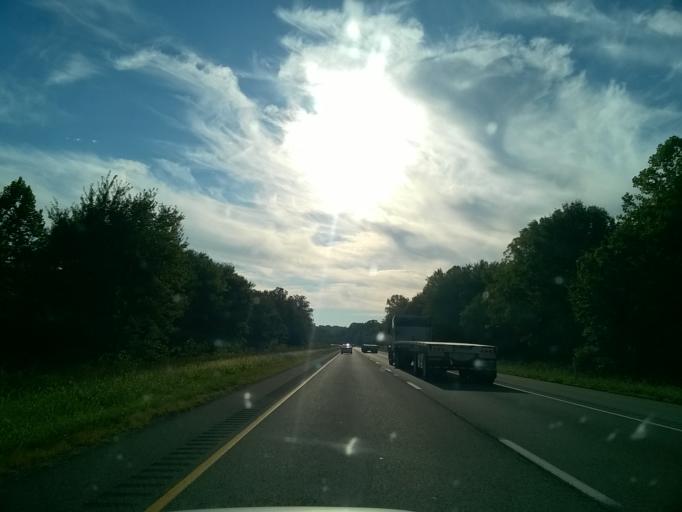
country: US
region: Indiana
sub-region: Spencer County
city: Dale
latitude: 38.1966
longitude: -87.1437
